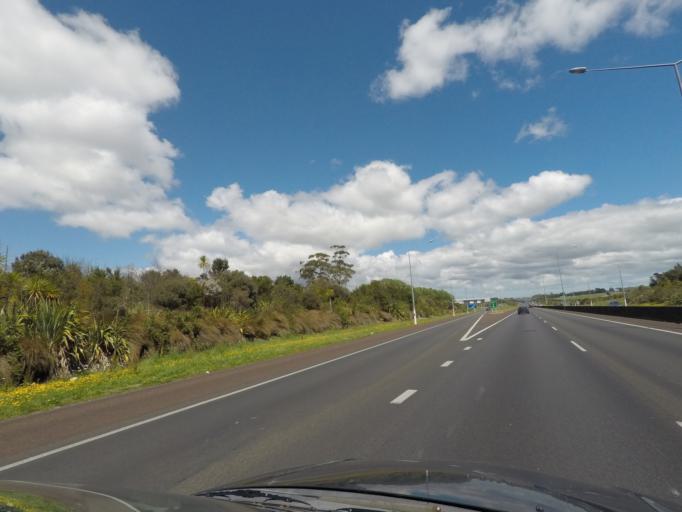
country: NZ
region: Auckland
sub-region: Auckland
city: Rosebank
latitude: -36.7975
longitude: 174.6430
